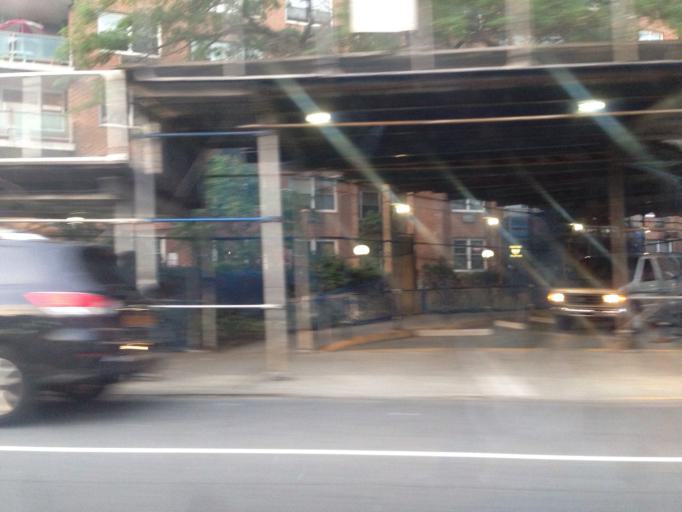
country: US
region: New York
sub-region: Kings County
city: Brooklyn
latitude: 40.6302
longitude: -73.9448
